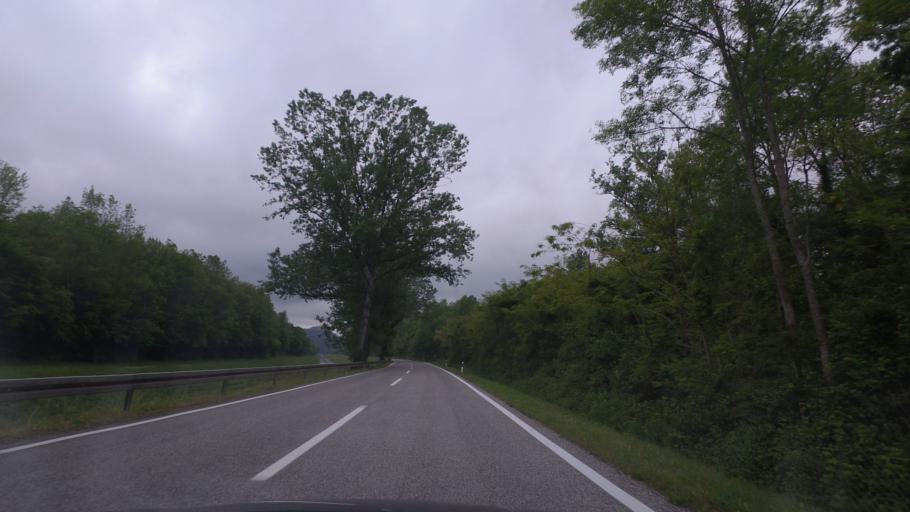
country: HR
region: Istarska
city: Karojba
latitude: 45.3653
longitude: 13.8692
